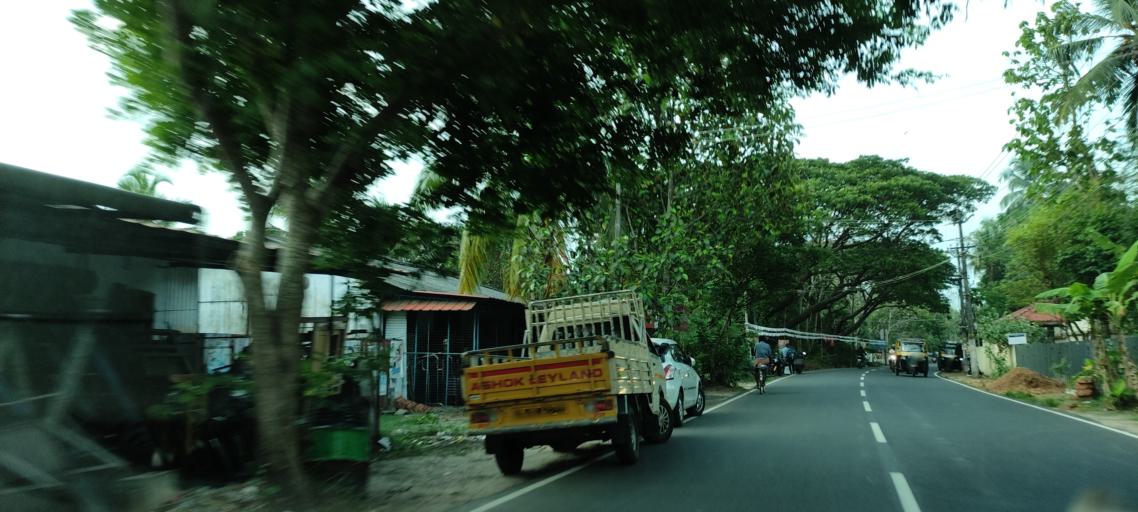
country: IN
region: Kerala
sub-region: Alappuzha
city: Kutiatodu
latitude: 9.7915
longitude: 76.3589
